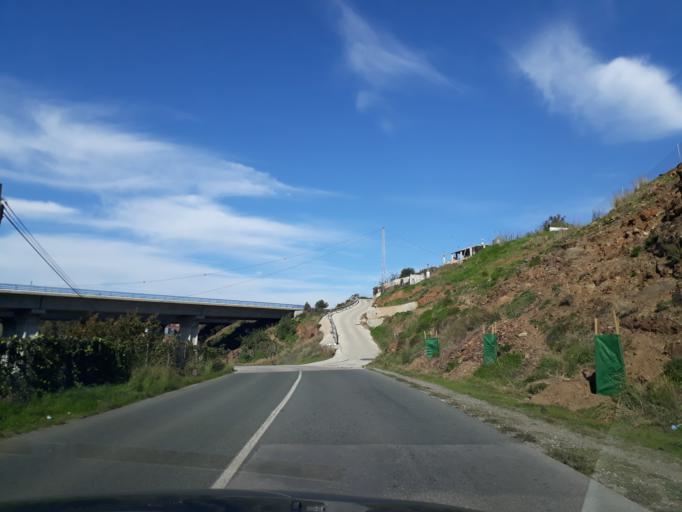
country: ES
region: Andalusia
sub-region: Provincia de Malaga
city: Fuengirola
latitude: 36.5215
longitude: -4.6847
